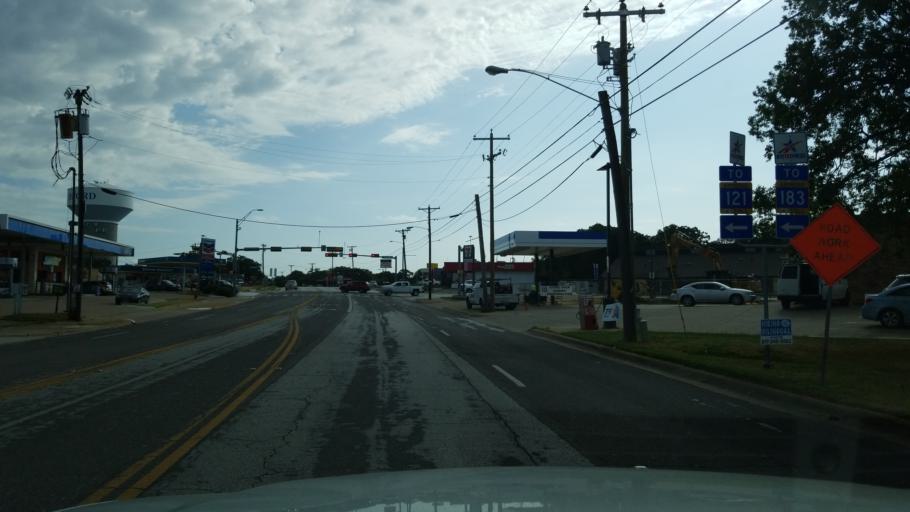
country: US
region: Texas
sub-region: Tarrant County
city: Hurst
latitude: 32.8341
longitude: -97.1626
